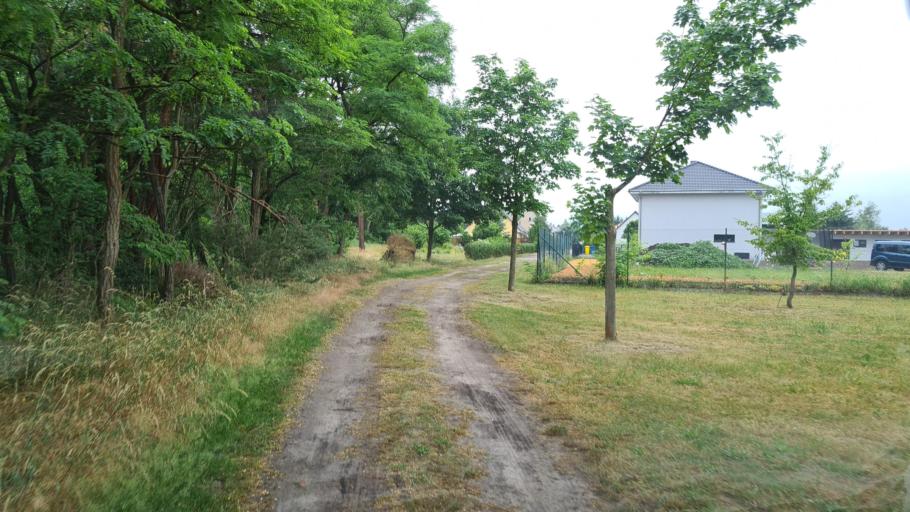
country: DE
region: Brandenburg
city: Tettau
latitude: 51.4251
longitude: 13.7337
